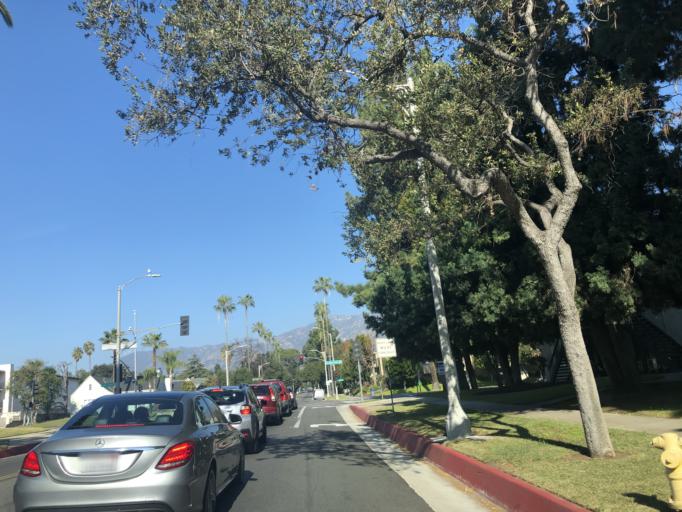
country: US
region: California
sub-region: Los Angeles County
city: Pasadena
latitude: 34.1572
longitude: -118.1214
